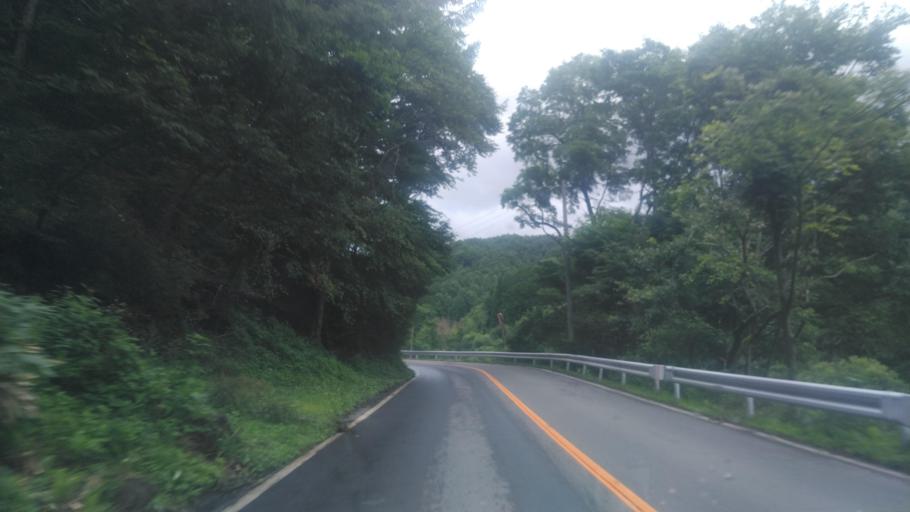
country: JP
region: Nagano
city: Ueda
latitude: 36.4899
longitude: 138.3704
